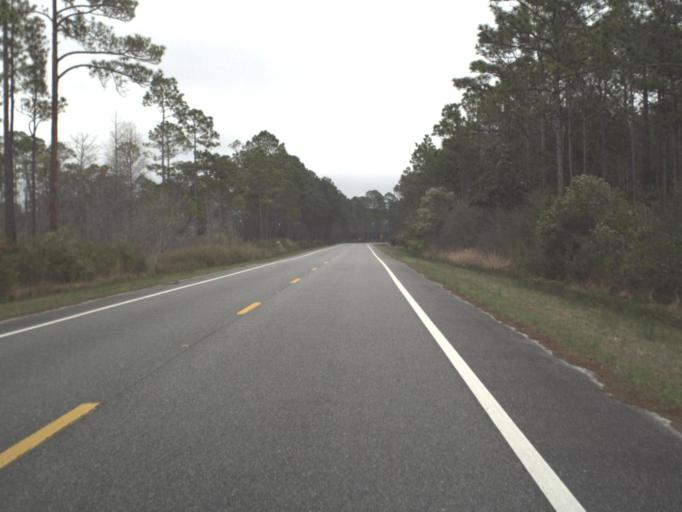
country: US
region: Florida
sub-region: Franklin County
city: Eastpoint
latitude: 29.8287
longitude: -84.8656
